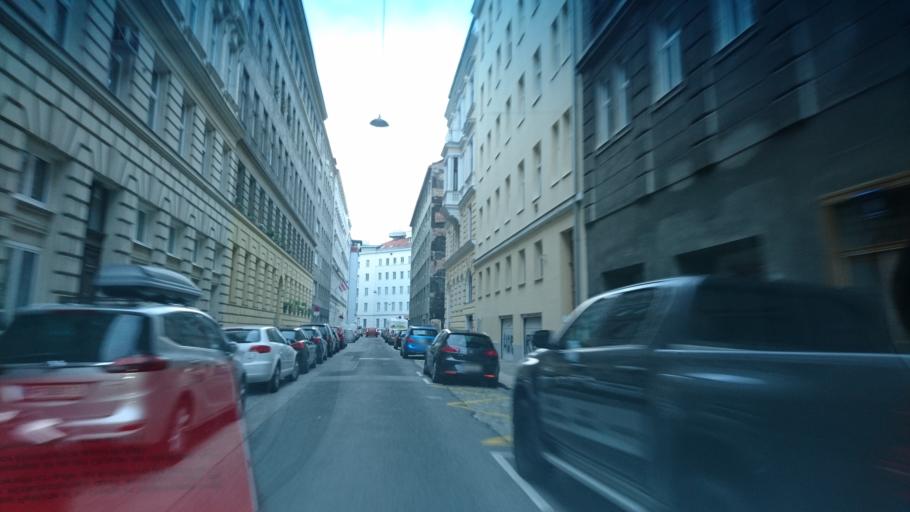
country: AT
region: Vienna
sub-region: Wien Stadt
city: Vienna
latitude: 48.2167
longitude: 16.3748
